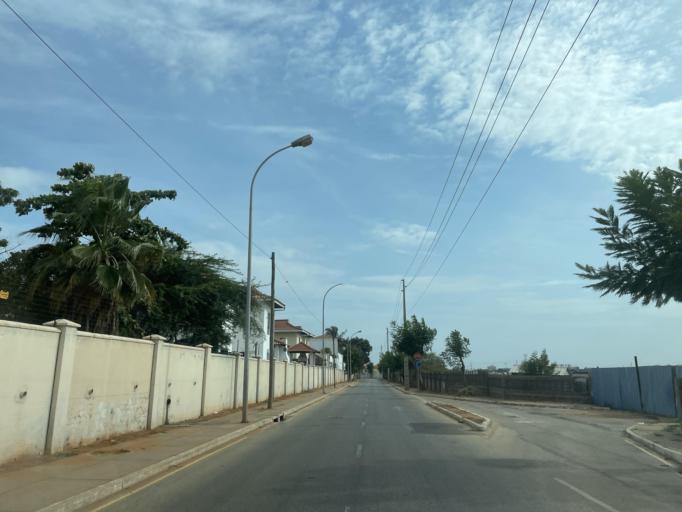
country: AO
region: Luanda
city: Luanda
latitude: -8.9260
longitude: 13.1789
